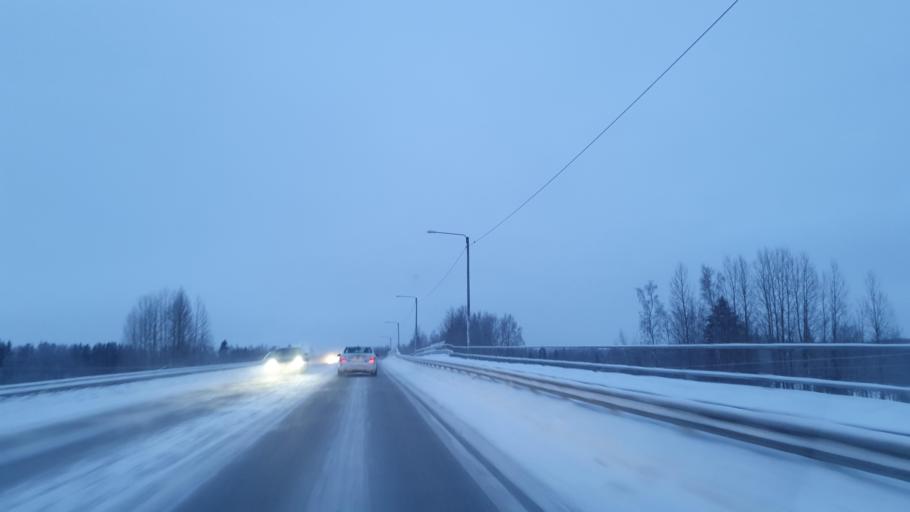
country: FI
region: Northern Ostrobothnia
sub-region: Oulu
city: Muhos
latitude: 64.8027
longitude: 26.0384
